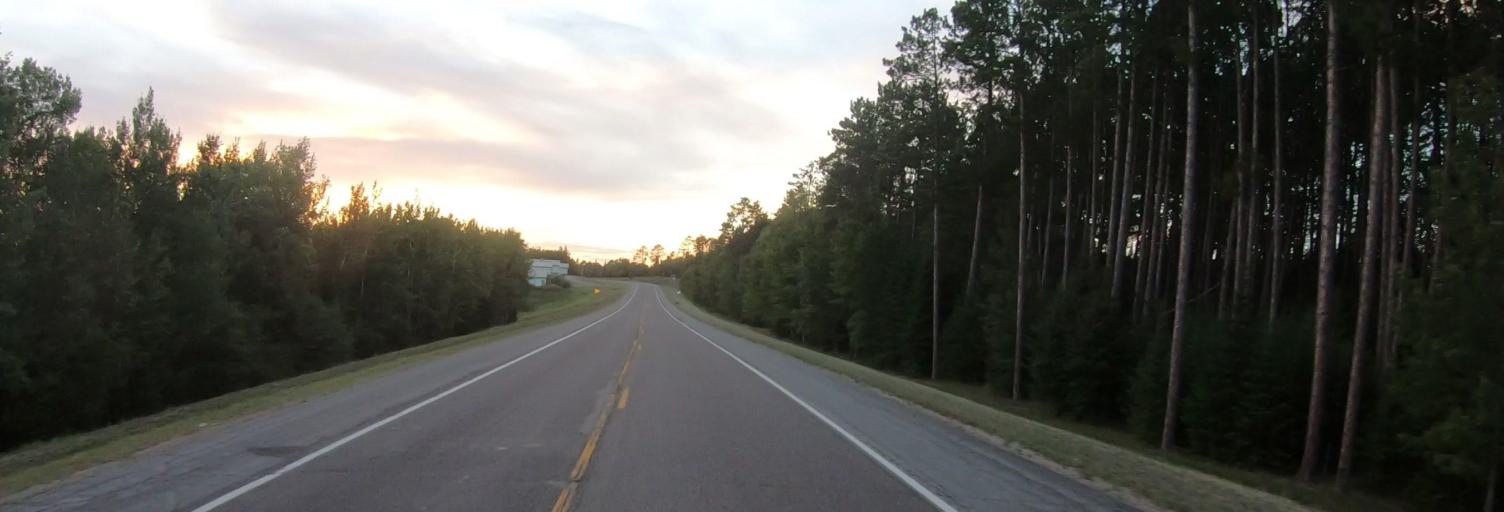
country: US
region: Minnesota
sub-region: Saint Louis County
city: Aurora
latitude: 47.8415
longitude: -92.3741
